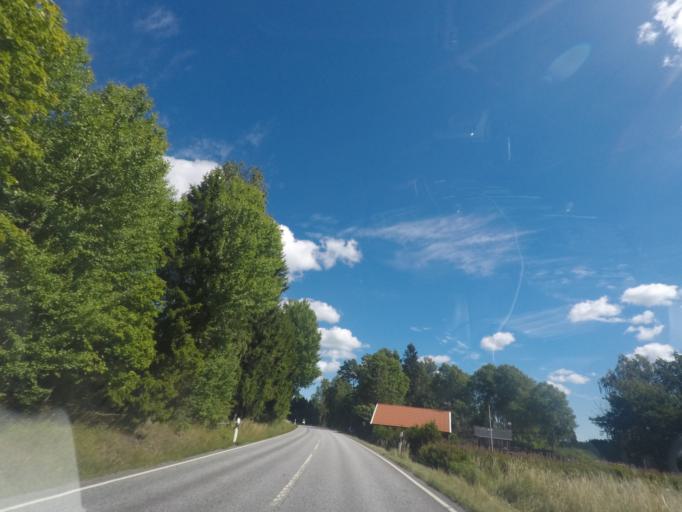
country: SE
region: Stockholm
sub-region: Norrtalje Kommun
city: Hallstavik
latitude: 59.9397
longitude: 18.7445
